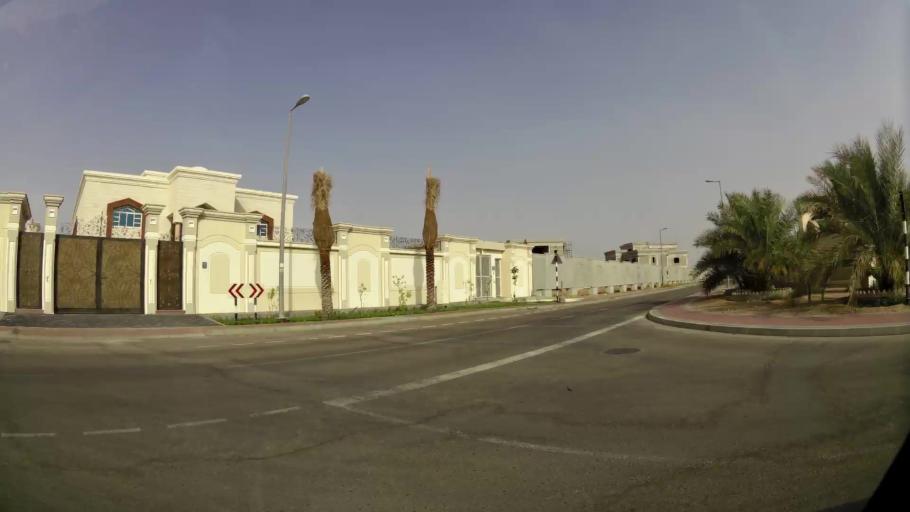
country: AE
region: Abu Dhabi
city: Al Ain
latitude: 24.1956
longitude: 55.6159
